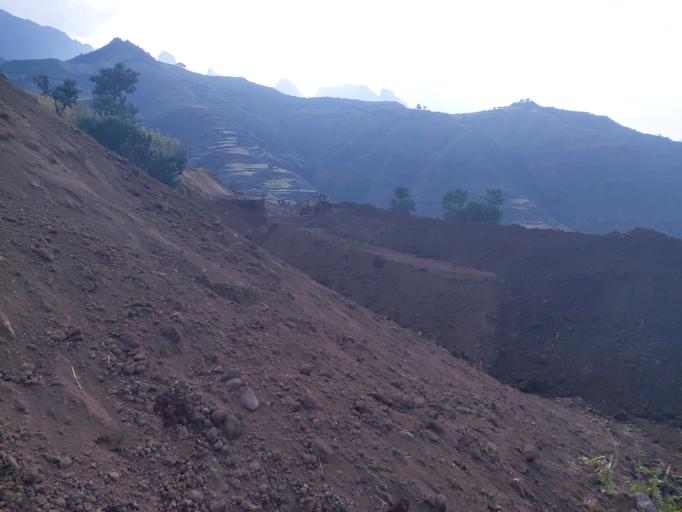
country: ET
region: Amhara
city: Debark'
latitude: 13.4002
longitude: 38.2207
